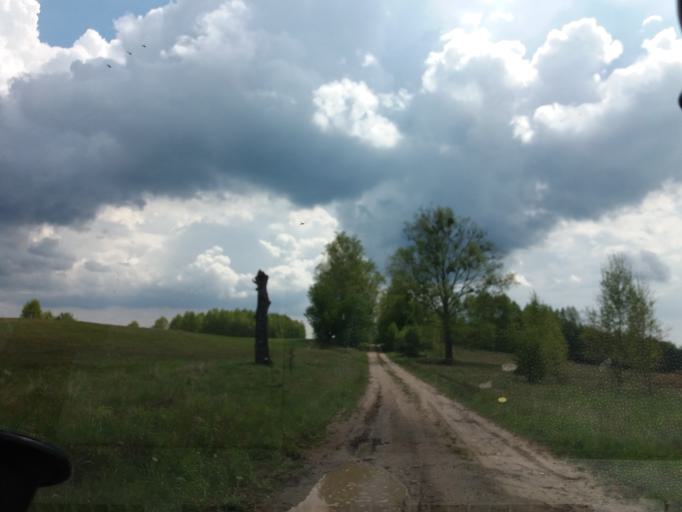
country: PL
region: West Pomeranian Voivodeship
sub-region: Powiat choszczenski
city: Drawno
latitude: 53.1373
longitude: 15.8376
